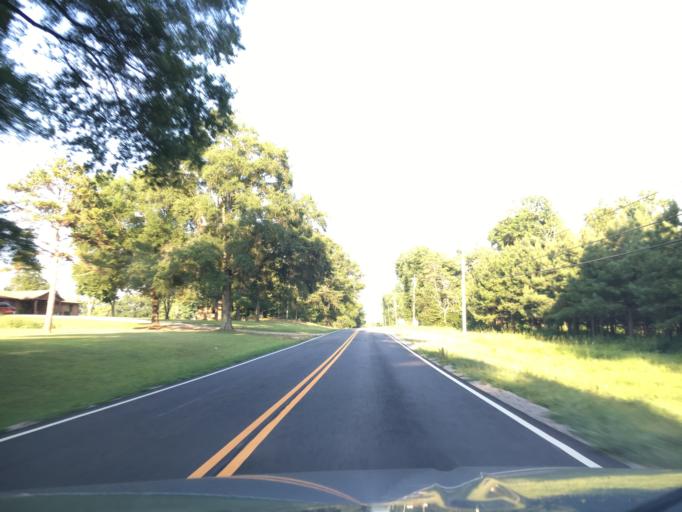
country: US
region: Virginia
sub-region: Pittsylvania County
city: Chatham
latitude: 36.8183
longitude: -79.3586
